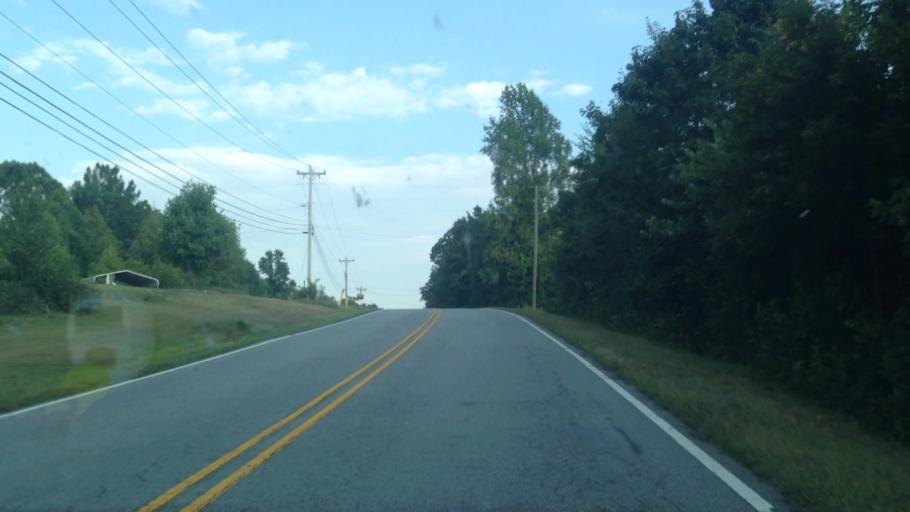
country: US
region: North Carolina
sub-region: Guilford County
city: High Point
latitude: 35.9629
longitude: -80.0774
